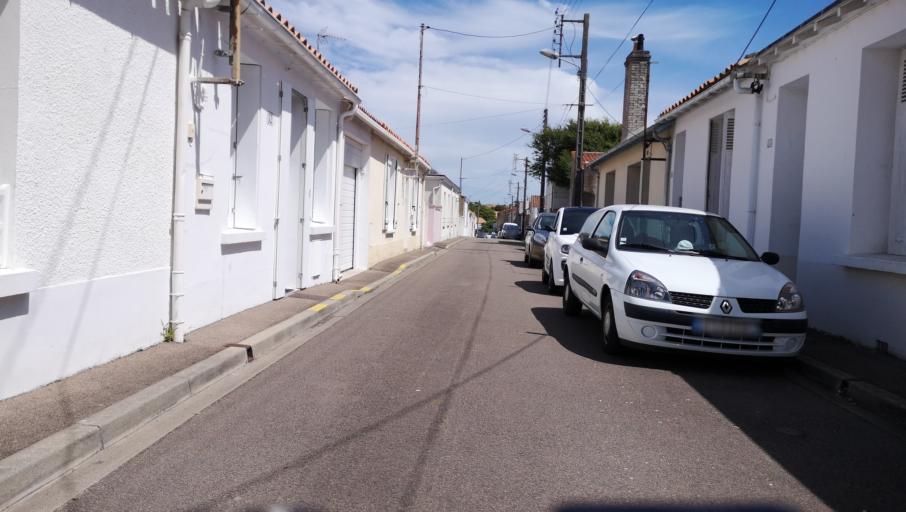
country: FR
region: Pays de la Loire
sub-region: Departement de la Vendee
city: Les Sables-d'Olonne
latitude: 46.5019
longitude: -1.7751
